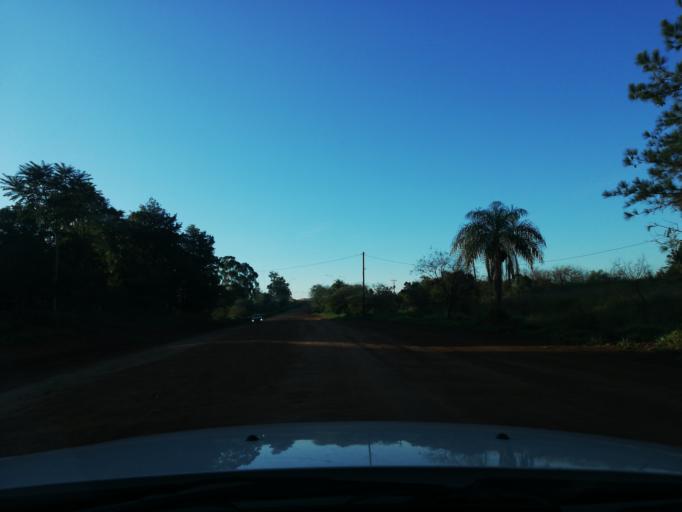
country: AR
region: Misiones
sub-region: Departamento de Capital
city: Posadas
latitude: -27.4682
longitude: -55.9708
